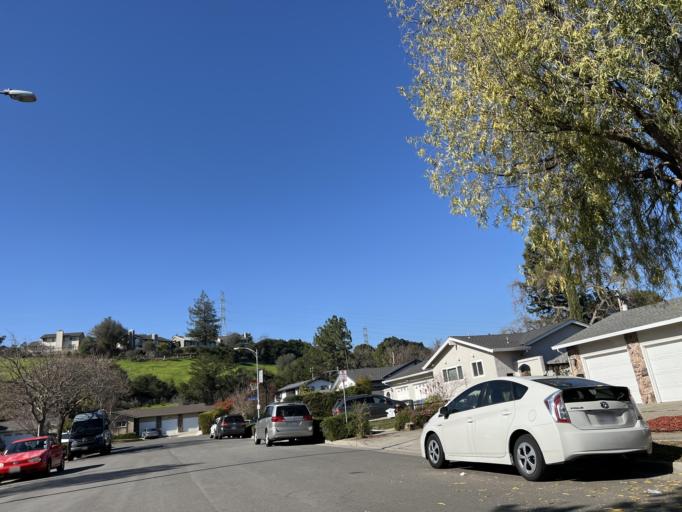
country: US
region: California
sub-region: Santa Clara County
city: Loyola
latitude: 37.3190
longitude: -122.0742
